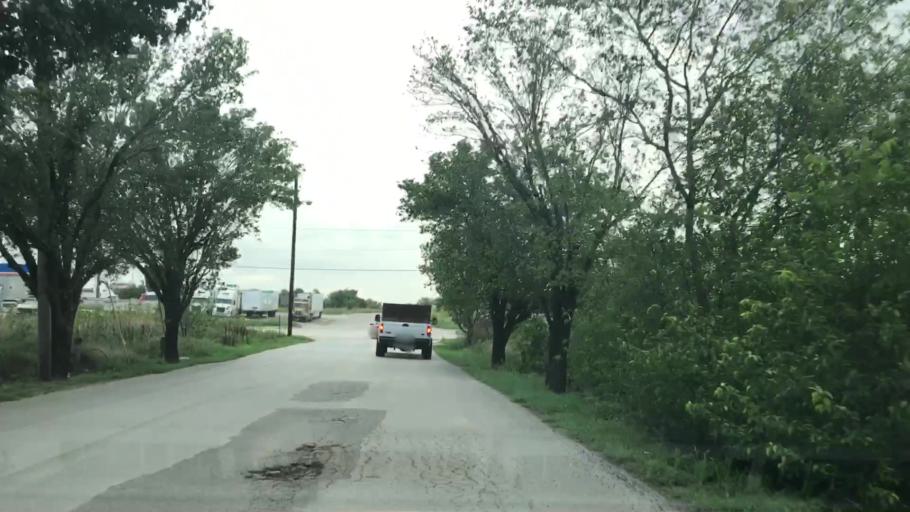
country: US
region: Texas
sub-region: Dallas County
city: Farmers Branch
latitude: 32.8817
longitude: -96.9006
